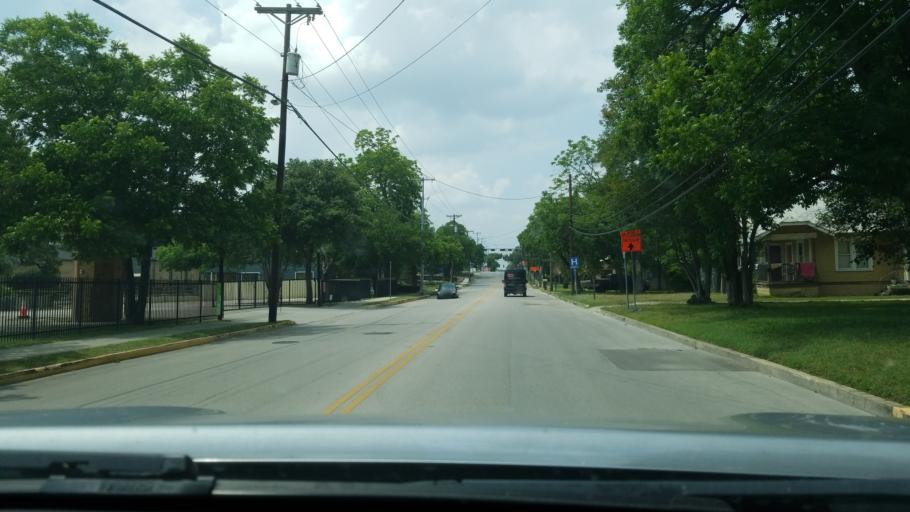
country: US
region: Texas
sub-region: Comal County
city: New Braunfels
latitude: 29.7067
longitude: -98.1175
